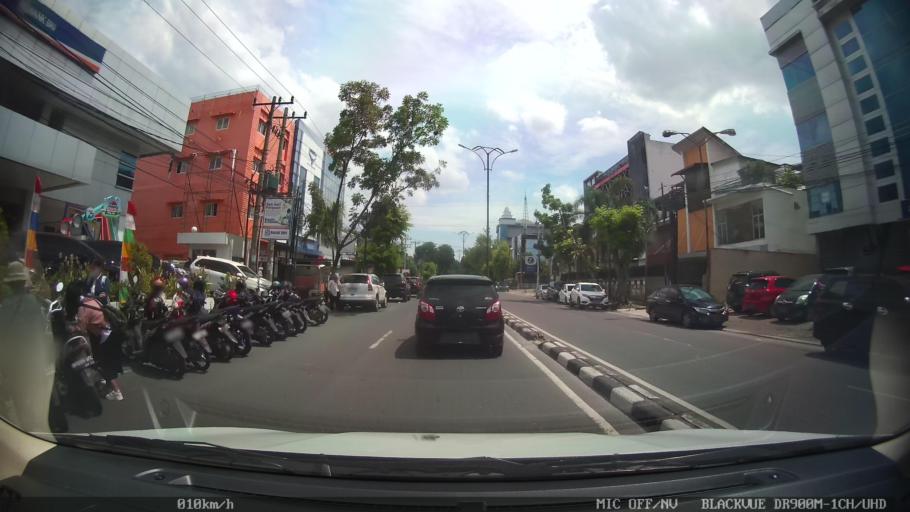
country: ID
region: North Sumatra
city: Medan
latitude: 3.5742
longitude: 98.6609
